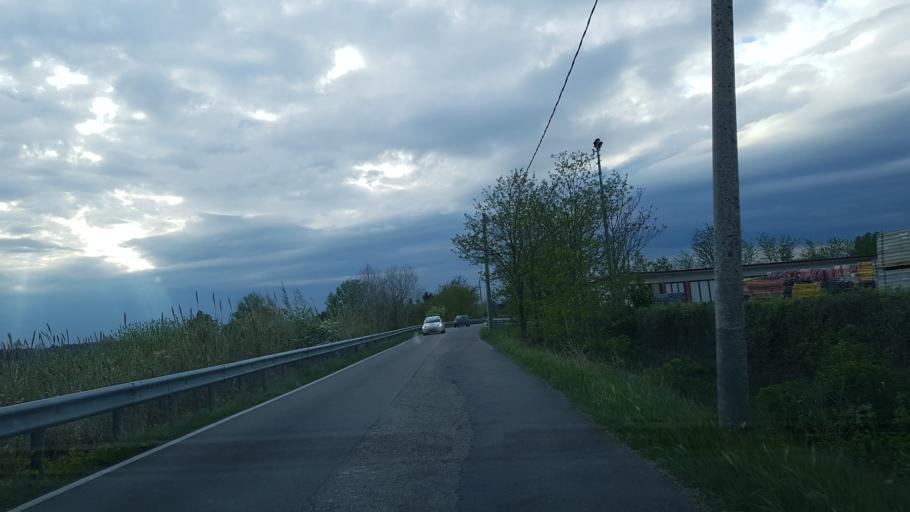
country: IT
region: Veneto
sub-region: Provincia di Verona
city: San Martino Buon Albergo
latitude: 45.4219
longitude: 11.0701
